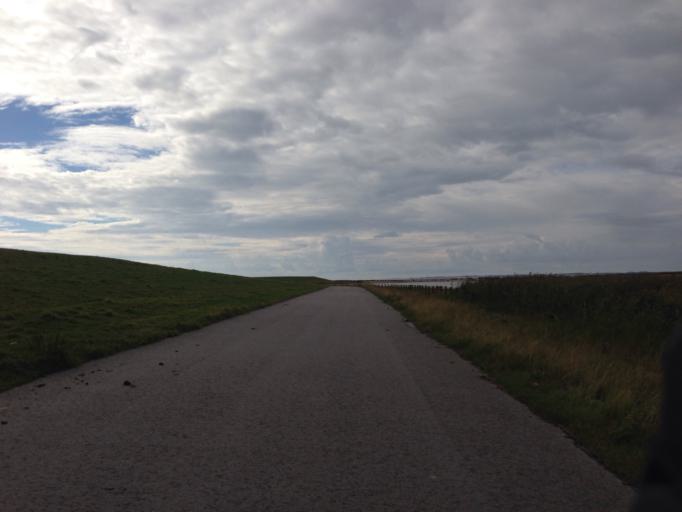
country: DE
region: Schleswig-Holstein
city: Oldsum
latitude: 54.7471
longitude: 8.4428
